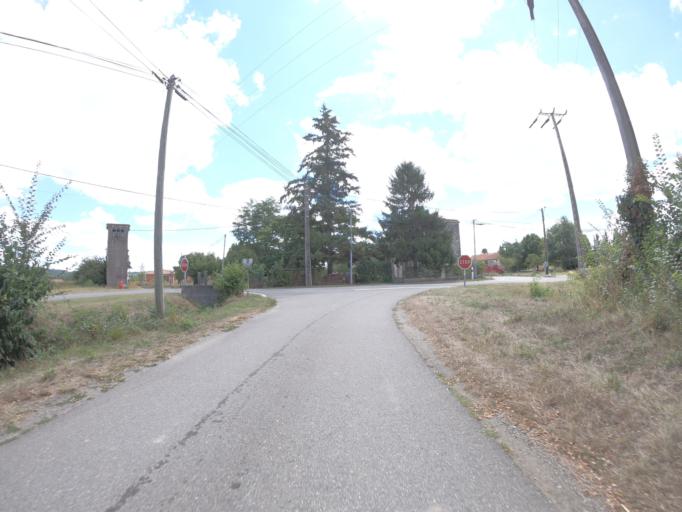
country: FR
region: Midi-Pyrenees
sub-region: Departement de l'Ariege
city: La Tour-du-Crieu
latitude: 43.0972
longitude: 1.7340
